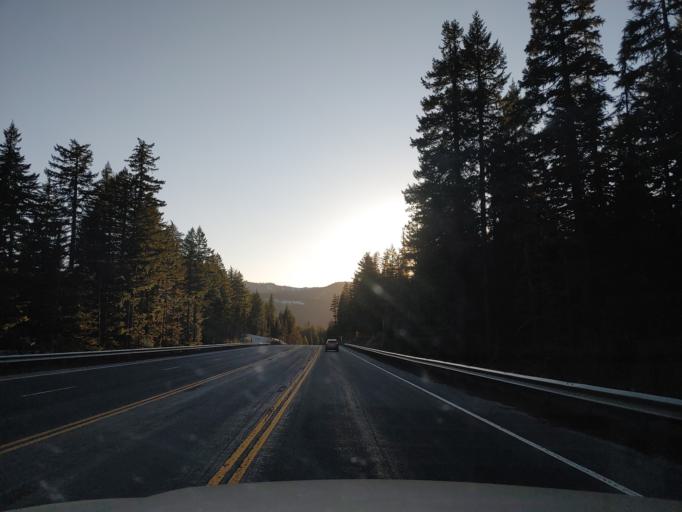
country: US
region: Oregon
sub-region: Lane County
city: Oakridge
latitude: 43.6113
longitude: -122.1141
